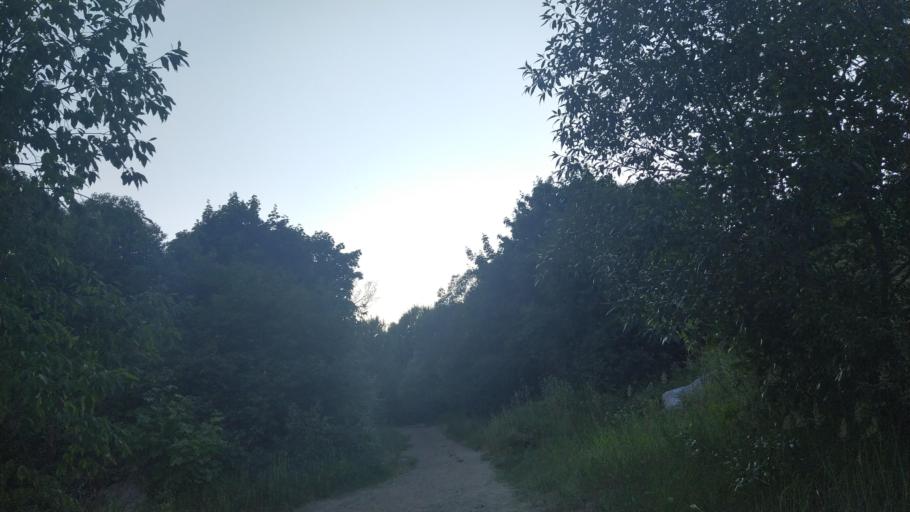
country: RU
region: St.-Petersburg
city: Kronshtadt
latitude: 60.0239
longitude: 29.6740
